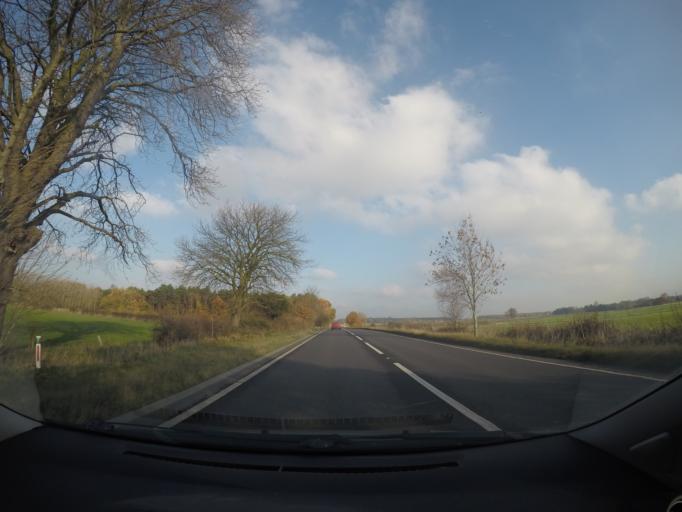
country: GB
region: England
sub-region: City of York
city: Murton
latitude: 54.0062
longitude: -1.0056
